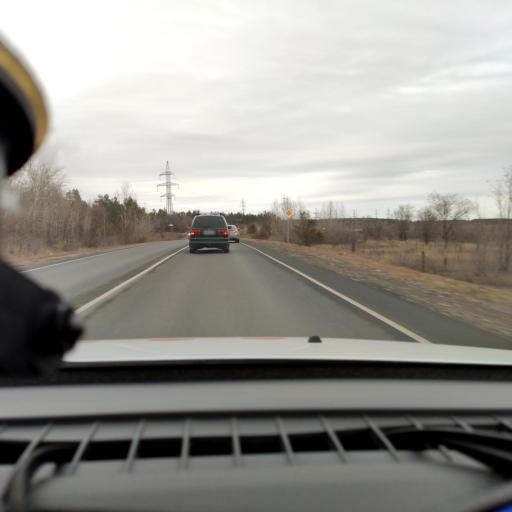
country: RU
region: Samara
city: Samara
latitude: 53.1234
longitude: 50.1976
